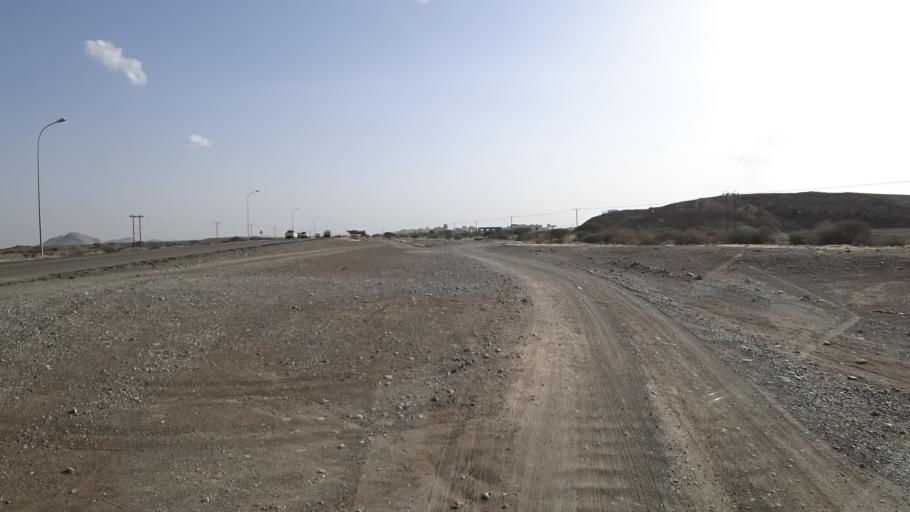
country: OM
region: Muhafazat ad Dakhiliyah
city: Izki
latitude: 22.8653
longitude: 57.7596
